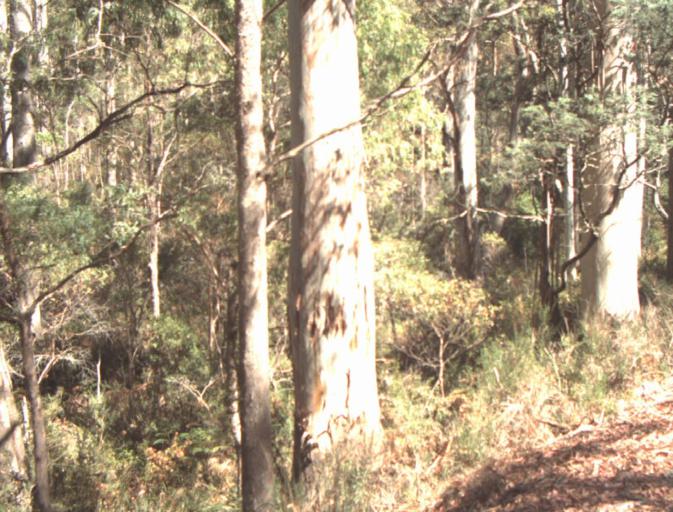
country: AU
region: Tasmania
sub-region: Launceston
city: Newstead
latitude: -41.3140
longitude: 147.3337
